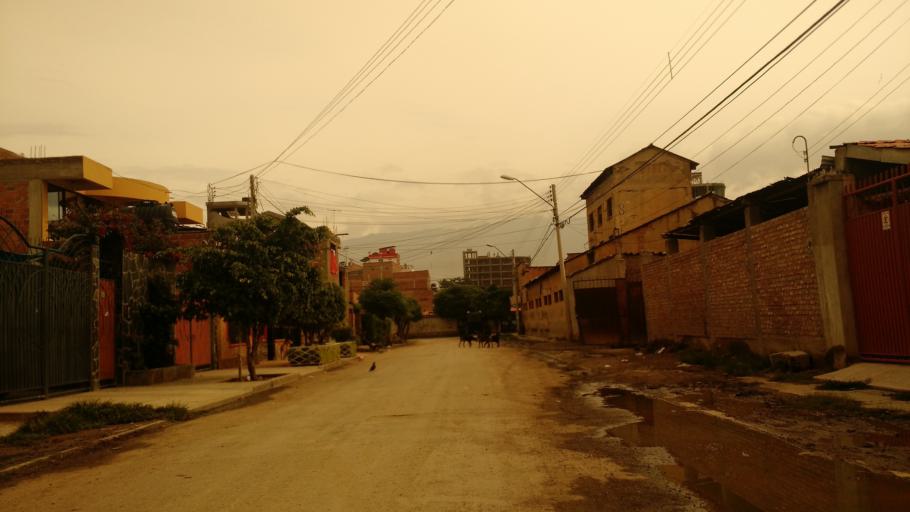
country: BO
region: Cochabamba
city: Cochabamba
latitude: -17.4163
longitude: -66.1561
